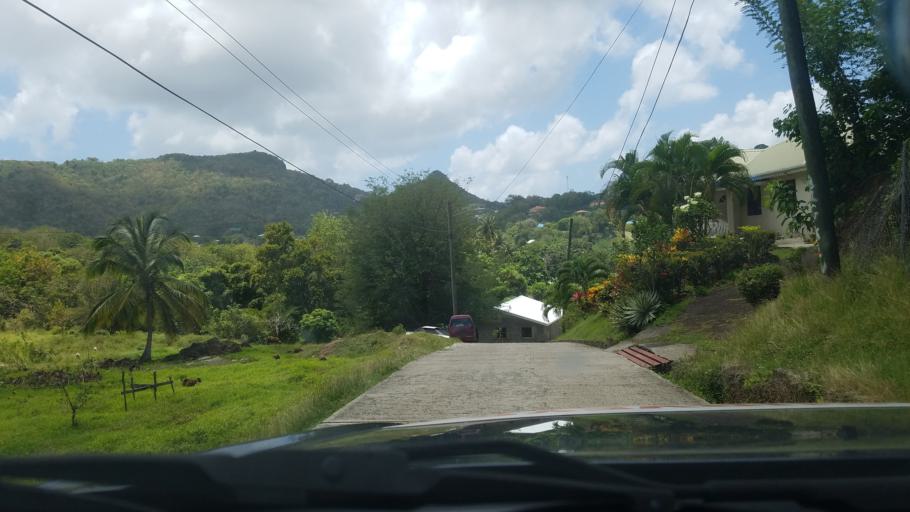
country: LC
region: Gros-Islet
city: Gros Islet
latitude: 14.0522
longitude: -60.9290
